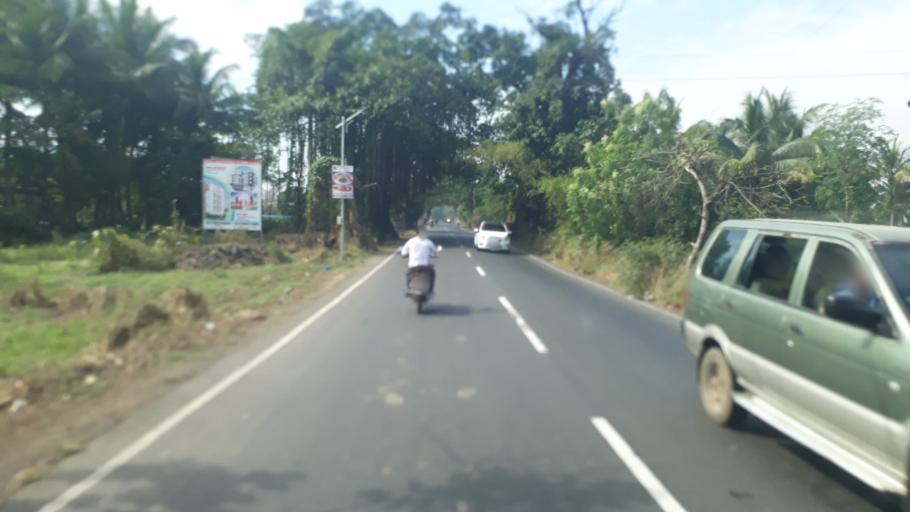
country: IN
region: Maharashtra
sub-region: Raigarh
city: Alibag
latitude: 18.6795
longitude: 72.9192
